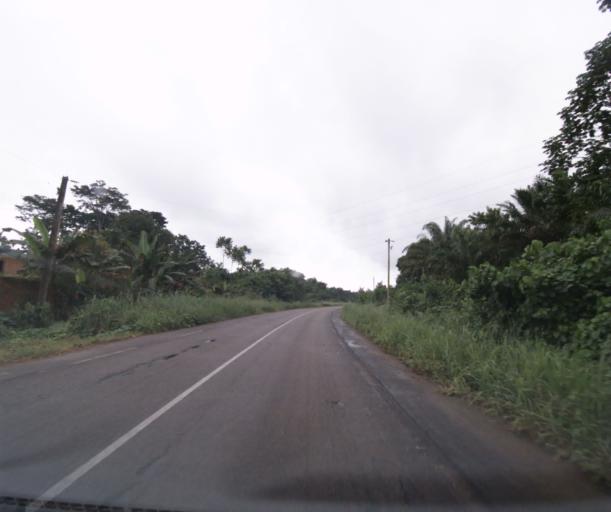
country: CM
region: Littoral
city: Dizangue
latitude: 3.5032
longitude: 10.1189
